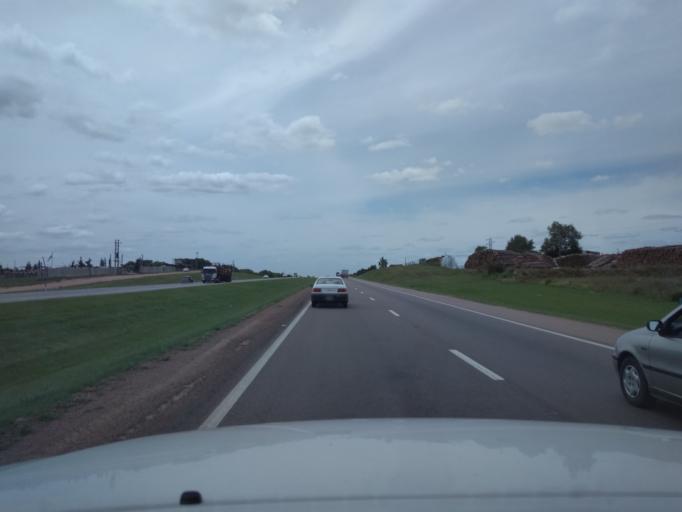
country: UY
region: Canelones
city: La Paz
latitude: -34.7447
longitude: -56.2525
